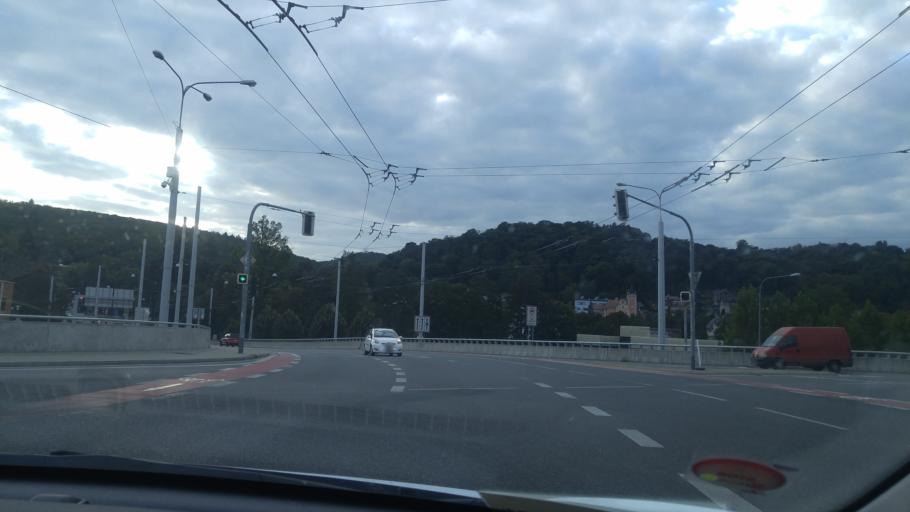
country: CZ
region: South Moravian
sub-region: Mesto Brno
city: Brno
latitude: 49.1940
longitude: 16.5696
